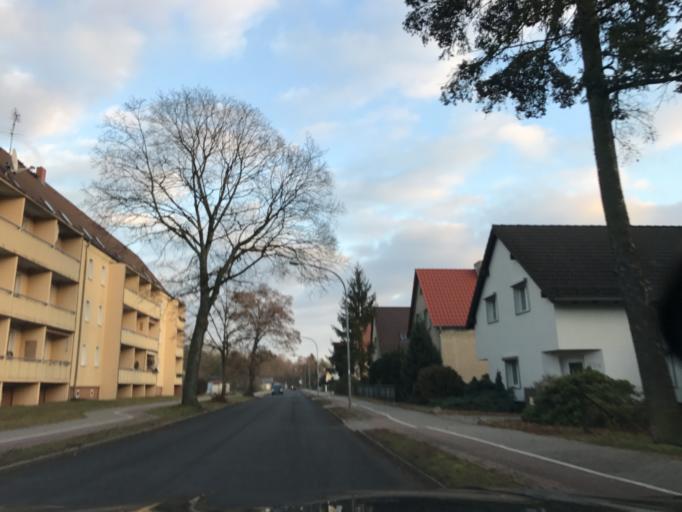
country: DE
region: Brandenburg
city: Wusterwitz
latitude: 52.3852
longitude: 12.3838
